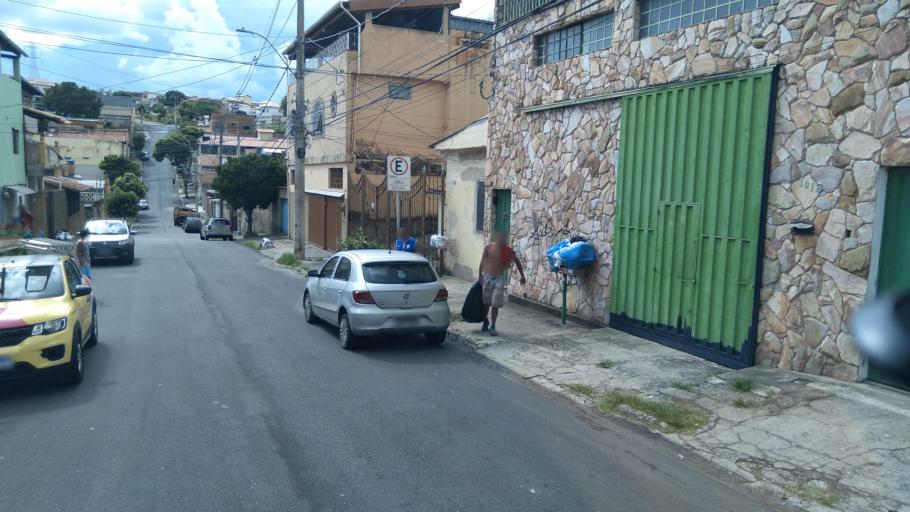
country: BR
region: Minas Gerais
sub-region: Belo Horizonte
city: Belo Horizonte
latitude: -19.8906
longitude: -43.8945
